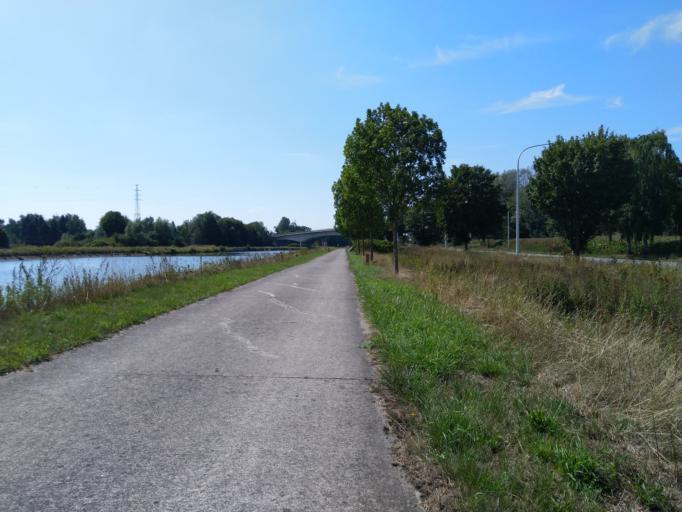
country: BE
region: Wallonia
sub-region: Province du Hainaut
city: Roeulx
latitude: 50.4726
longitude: 4.0424
